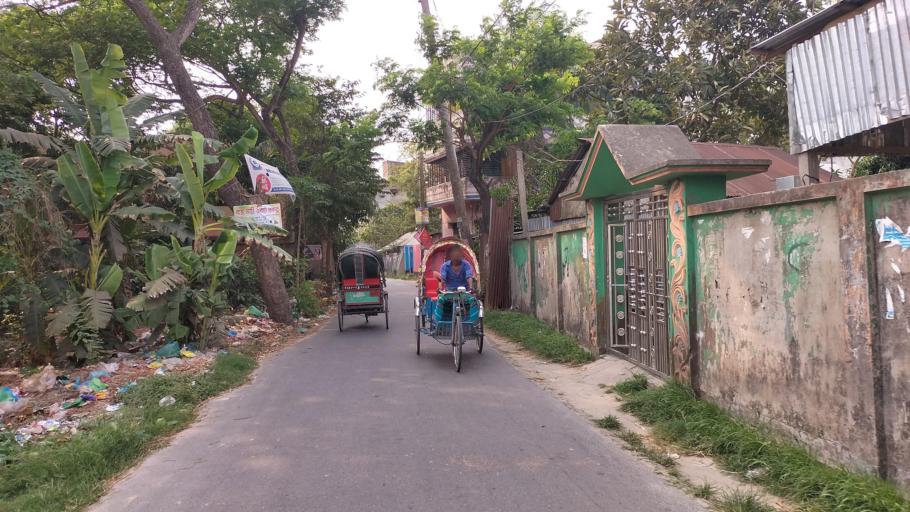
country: BD
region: Dhaka
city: Azimpur
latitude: 23.6704
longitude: 90.3445
